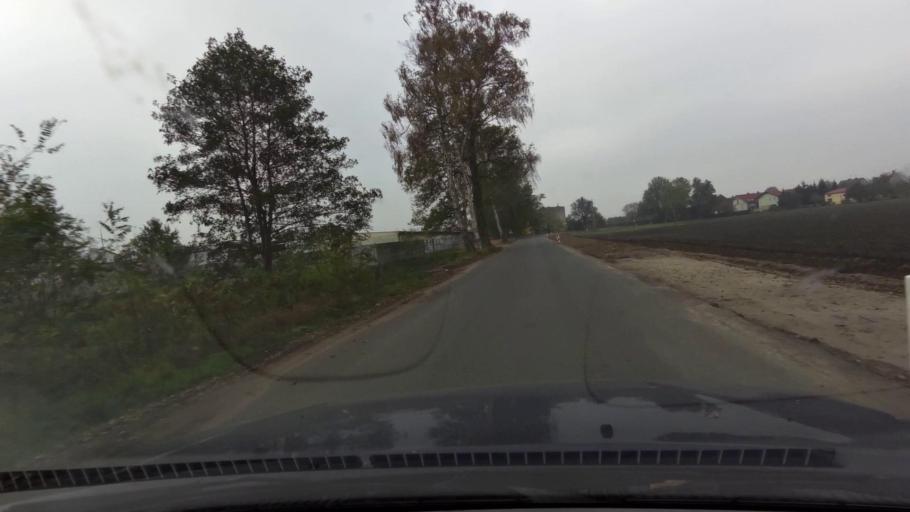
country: PL
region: West Pomeranian Voivodeship
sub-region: Powiat goleniowski
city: Goleniow
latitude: 53.5056
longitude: 14.7202
